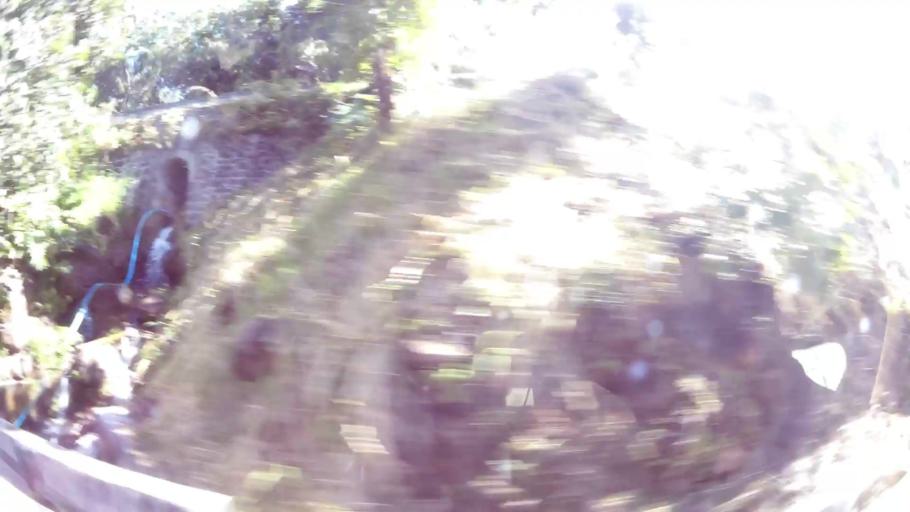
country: DM
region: Saint Paul
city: Pont Casse
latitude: 15.3465
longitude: -61.3683
